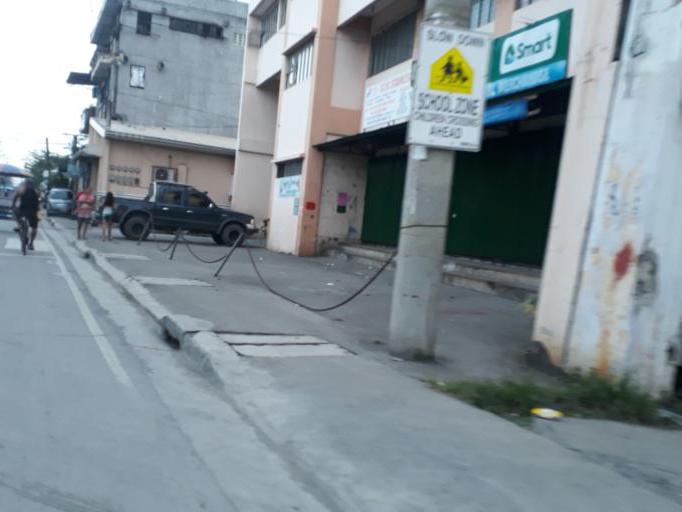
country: PH
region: Calabarzon
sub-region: Province of Rizal
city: Valenzuela
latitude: 14.6989
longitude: 120.9518
